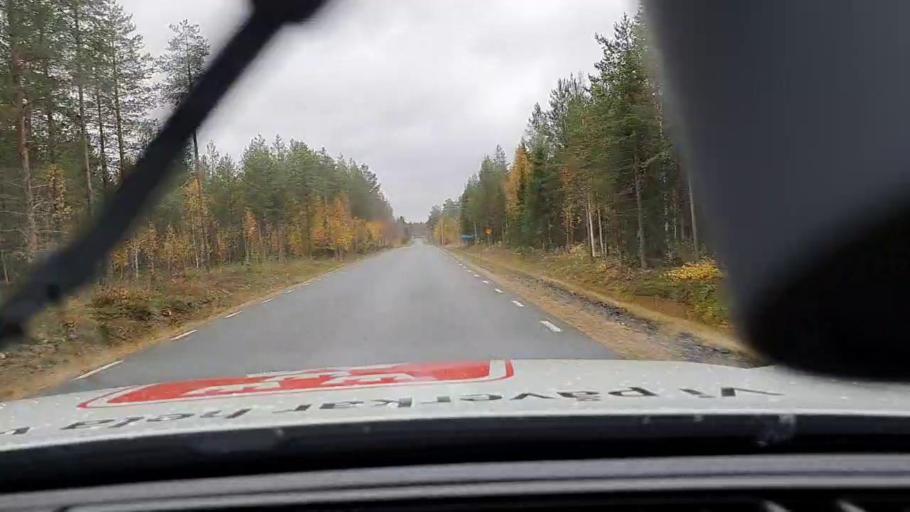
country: SE
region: Norrbotten
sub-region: Haparanda Kommun
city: Haparanda
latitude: 65.9420
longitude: 23.8014
